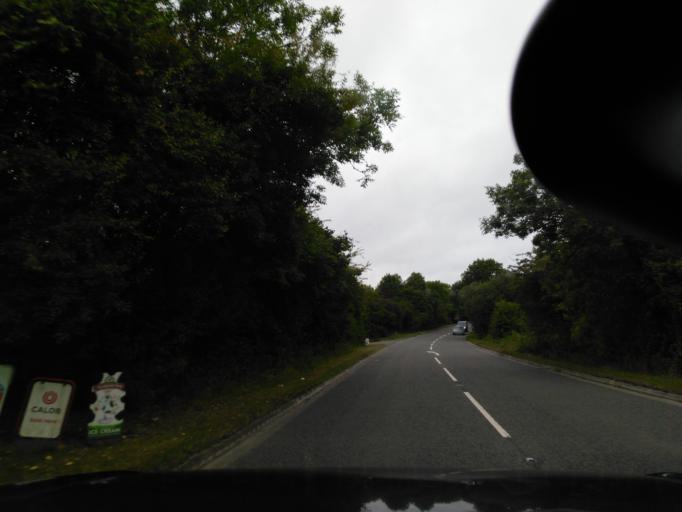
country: GB
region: England
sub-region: Wiltshire
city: Westbury
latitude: 51.2789
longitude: -2.1818
